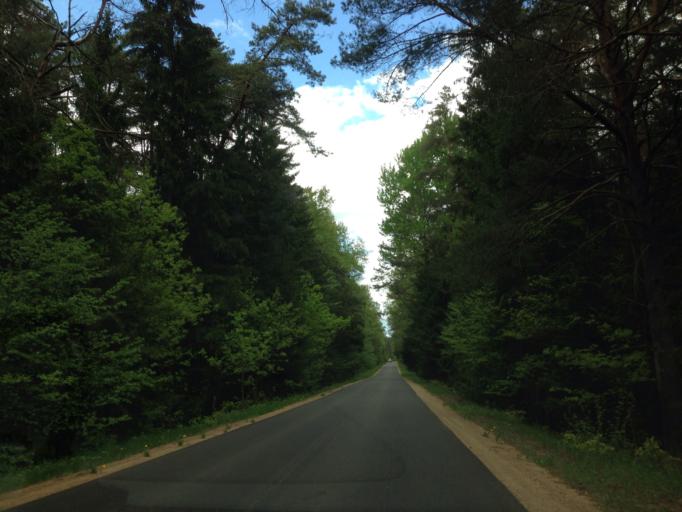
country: PL
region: Podlasie
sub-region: Powiat grajewski
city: Radzilow
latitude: 53.3426
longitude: 22.5979
